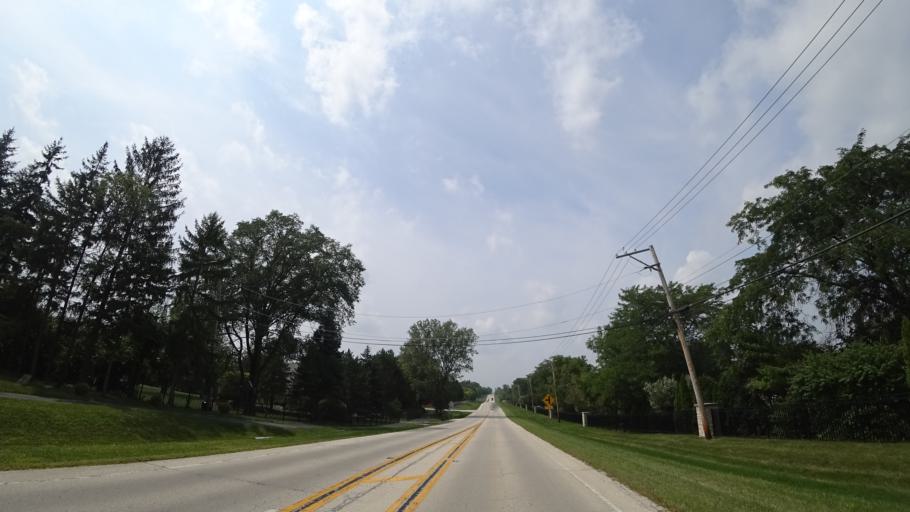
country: US
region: Illinois
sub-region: Will County
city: Goodings Grove
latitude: 41.6151
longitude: -87.9018
